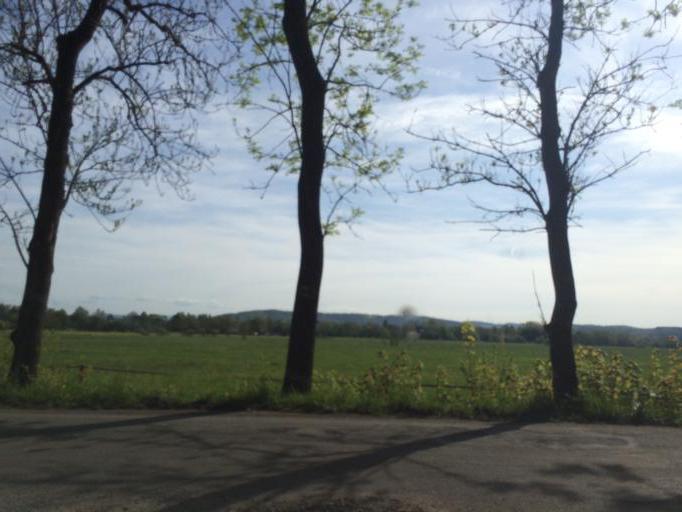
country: CZ
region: Central Bohemia
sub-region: Okres Mlada Boleslav
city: Zd'ar
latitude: 50.5424
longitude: 15.0683
